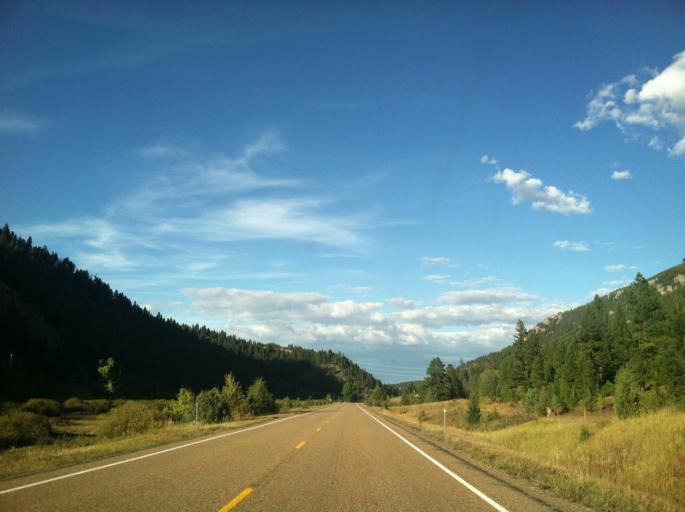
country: US
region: Montana
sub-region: Granite County
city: Philipsburg
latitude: 46.4338
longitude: -113.2684
